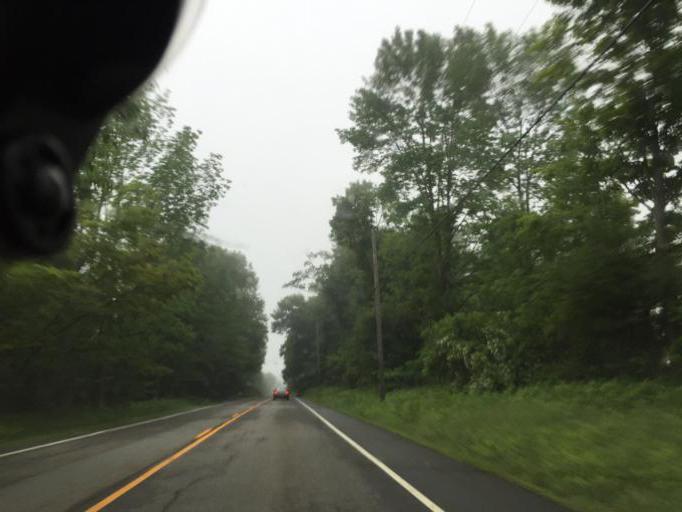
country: US
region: Connecticut
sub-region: Litchfield County
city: Winchester Center
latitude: 41.8733
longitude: -73.2495
